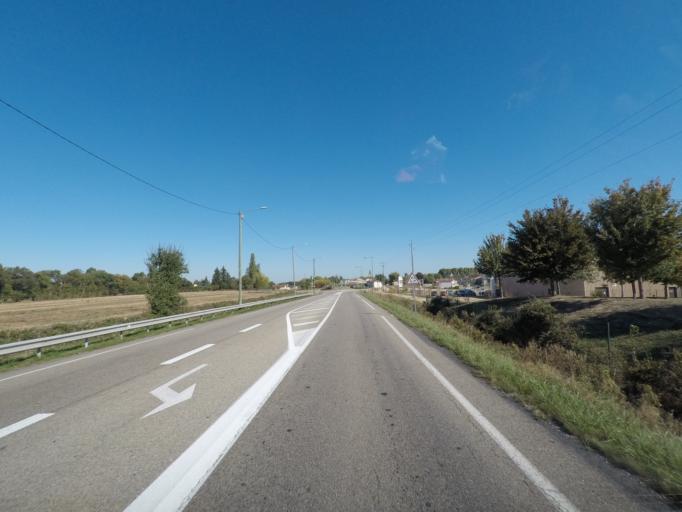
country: FR
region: Rhone-Alpes
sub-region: Departement de l'Ain
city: Servas
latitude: 46.1277
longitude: 5.1610
